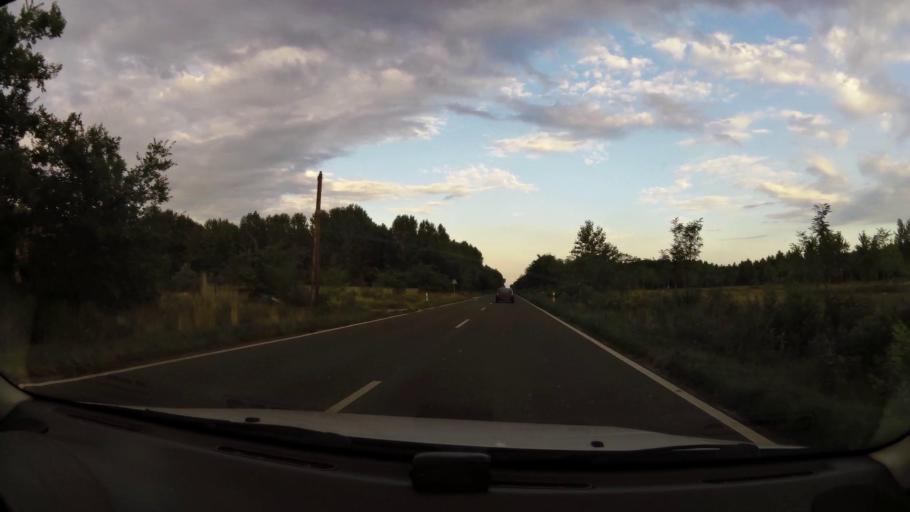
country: HU
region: Pest
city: Tapioszele
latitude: 47.2993
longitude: 19.8919
